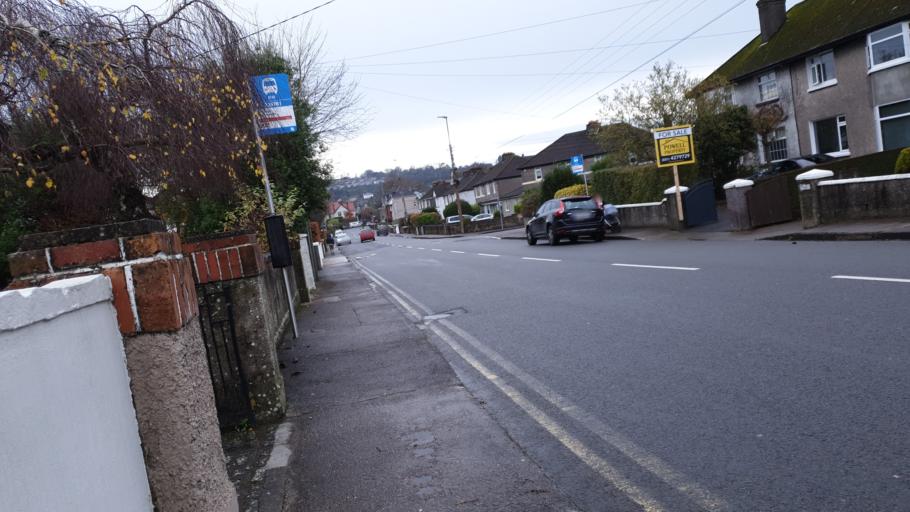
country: IE
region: Munster
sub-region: County Cork
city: Cork
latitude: 51.8941
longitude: -8.4306
